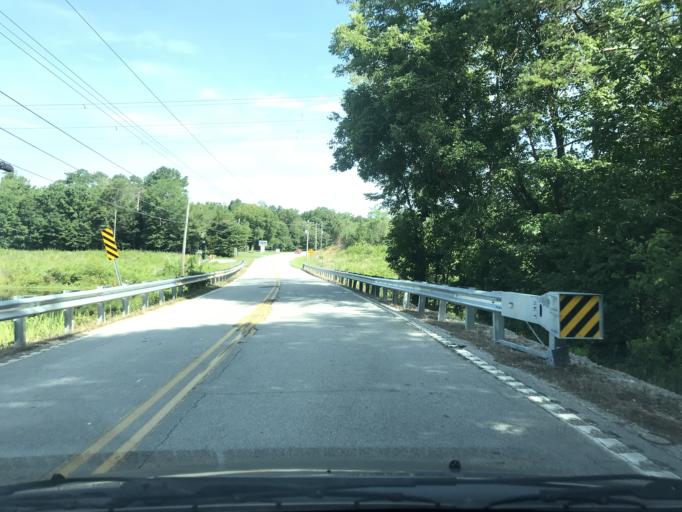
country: US
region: Tennessee
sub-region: Hamilton County
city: Lakesite
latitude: 35.2512
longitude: -85.0673
